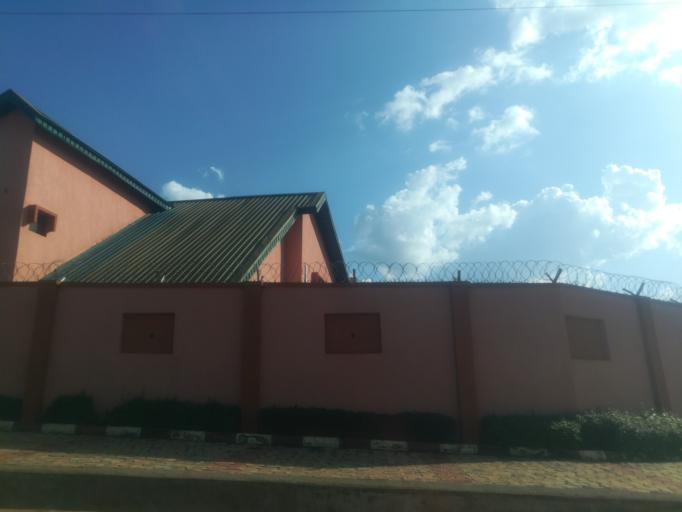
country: NG
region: Oyo
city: Ibadan
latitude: 7.4385
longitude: 3.9656
